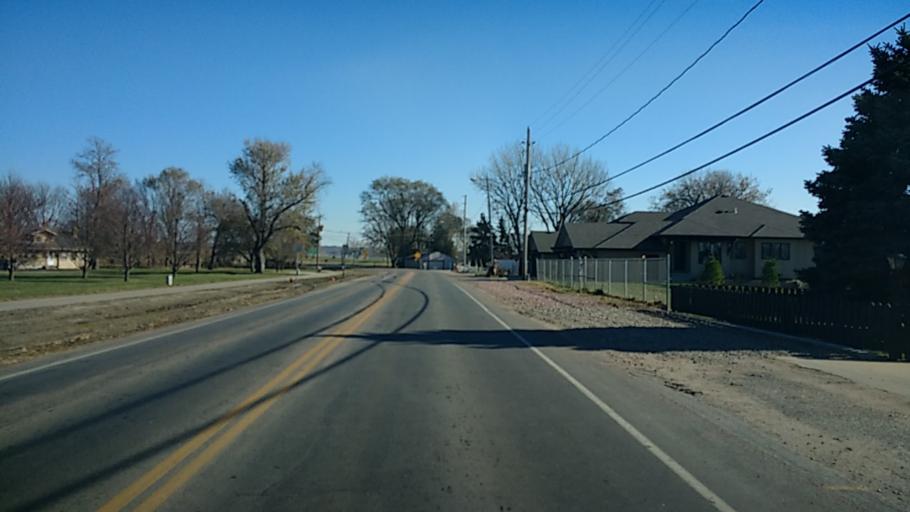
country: US
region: South Dakota
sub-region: Union County
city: North Sioux City
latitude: 42.5507
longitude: -96.5134
